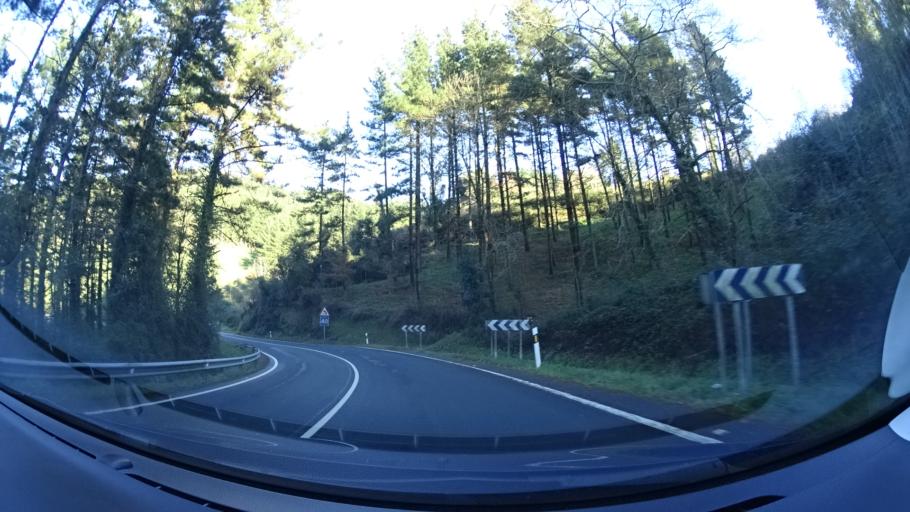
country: ES
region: Basque Country
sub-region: Bizkaia
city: Berriatua
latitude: 43.3152
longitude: -2.4787
